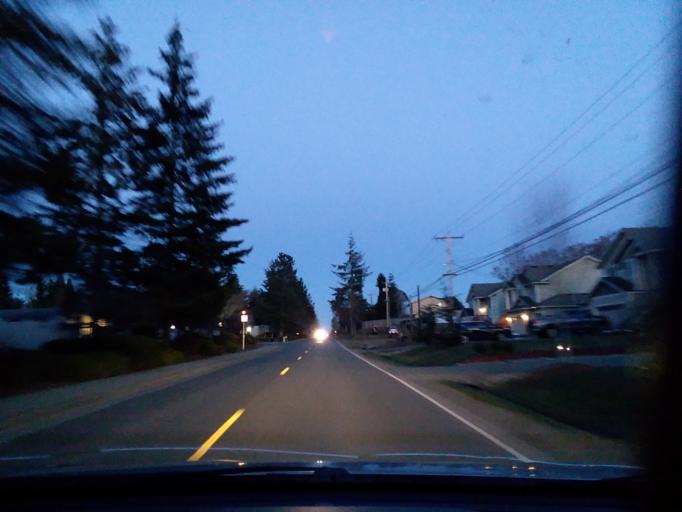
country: US
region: Washington
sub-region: Snohomish County
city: Martha Lake
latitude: 47.9074
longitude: -122.2551
